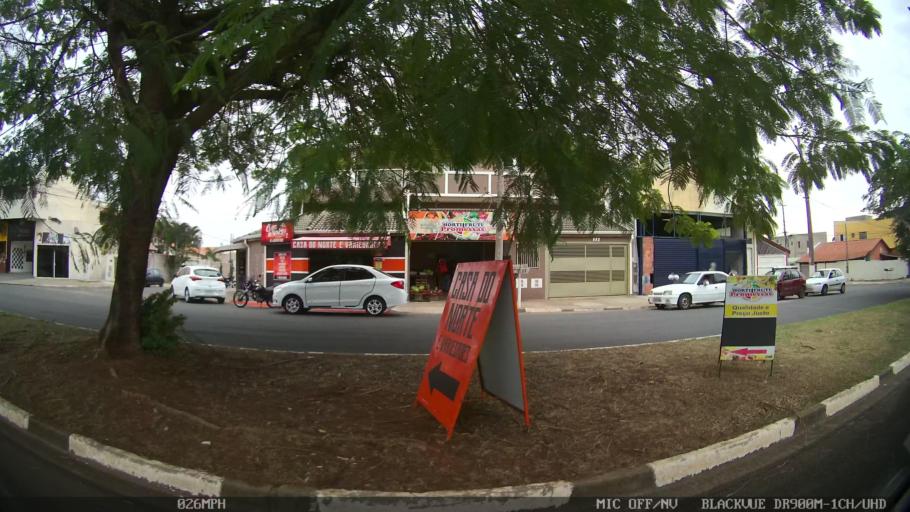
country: BR
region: Sao Paulo
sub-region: Paulinia
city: Paulinia
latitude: -22.7174
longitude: -47.1720
